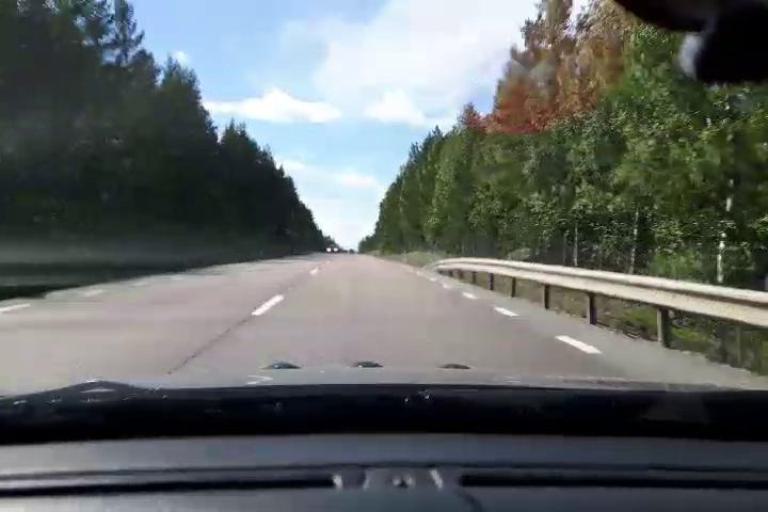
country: SE
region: Gaevleborg
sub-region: Bollnas Kommun
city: Bollnas
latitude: 61.2979
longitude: 16.4847
